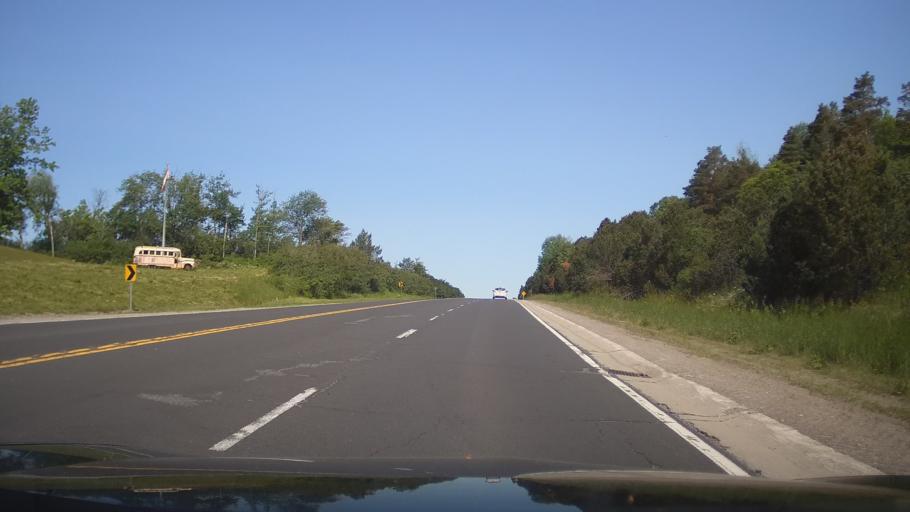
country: CA
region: Ontario
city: Omemee
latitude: 44.2927
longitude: -78.5905
